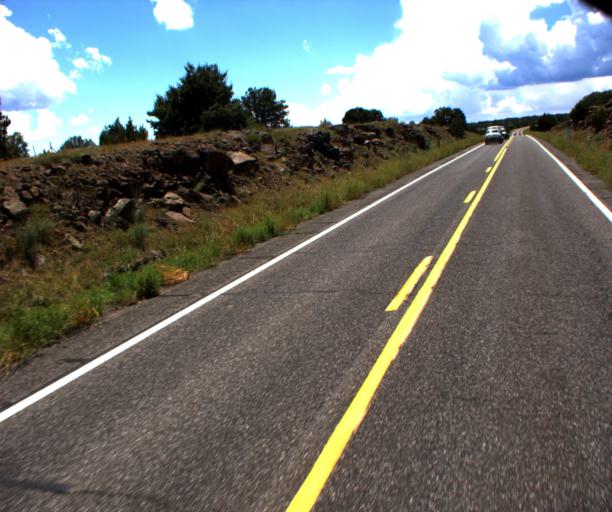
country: US
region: Arizona
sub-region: Gila County
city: Pine
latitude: 34.4926
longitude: -111.5924
